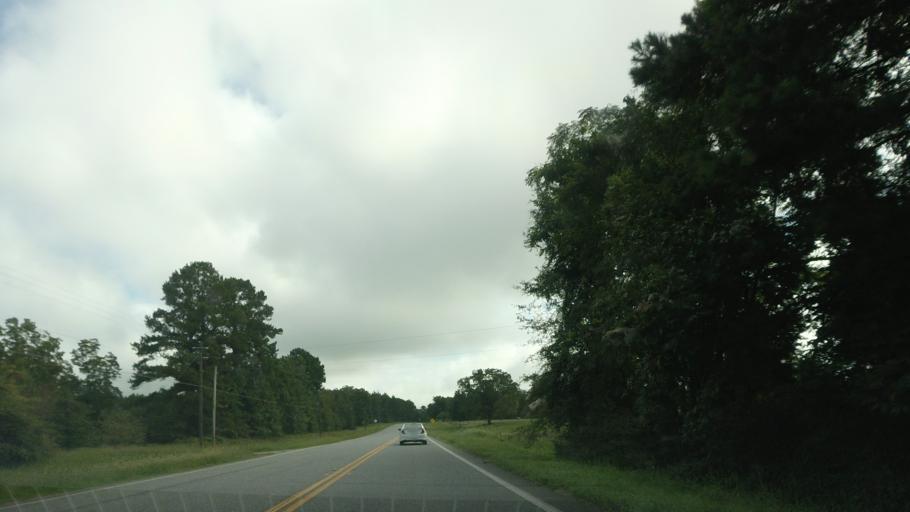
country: US
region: Georgia
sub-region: Laurens County
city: Dublin
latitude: 32.5487
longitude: -83.0127
